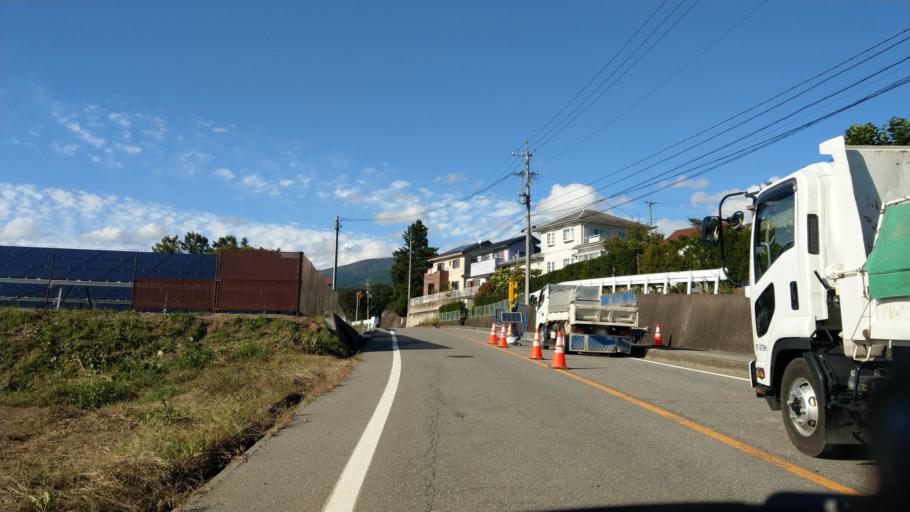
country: JP
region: Nagano
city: Komoro
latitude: 36.3374
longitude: 138.4278
